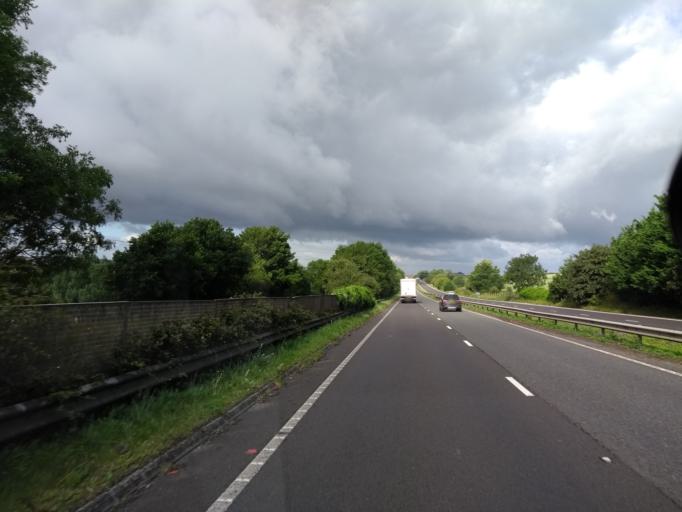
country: GB
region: England
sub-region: Somerset
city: Wincanton
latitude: 51.0417
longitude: -2.4632
